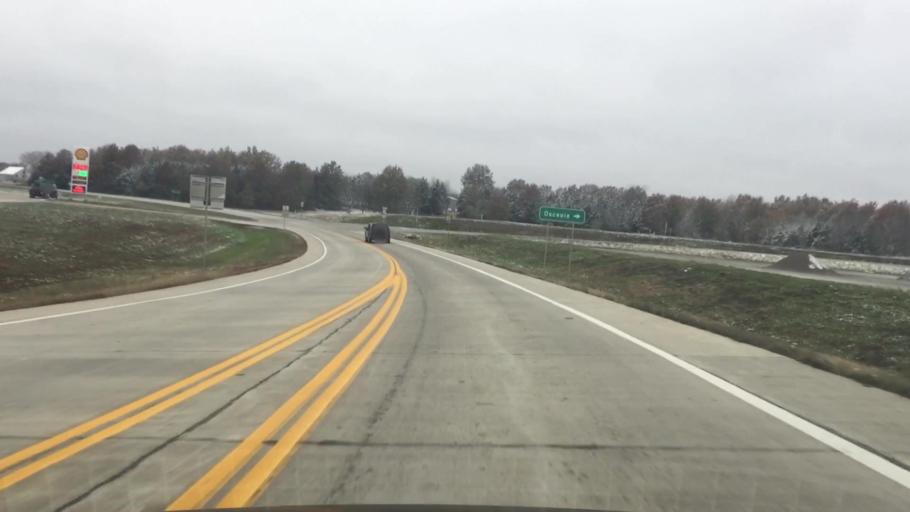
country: US
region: Missouri
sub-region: Saint Clair County
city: Osceola
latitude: 38.0398
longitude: -93.6836
